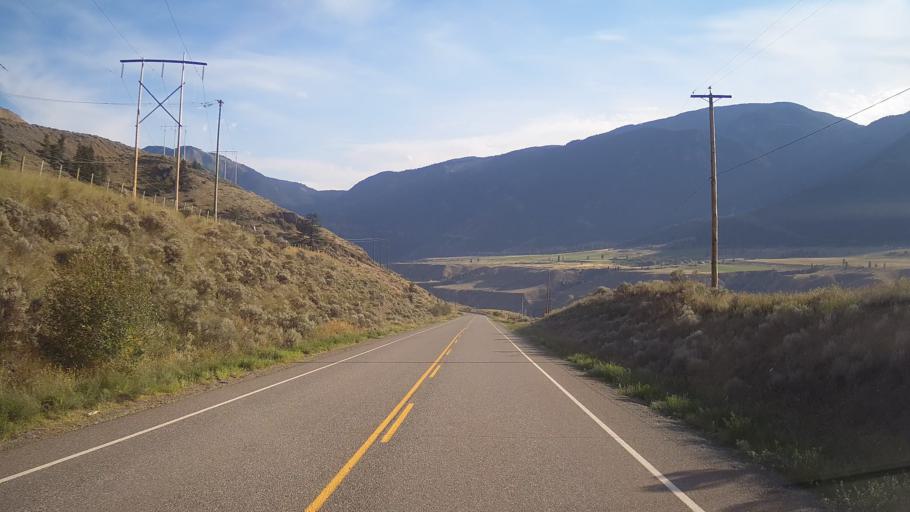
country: CA
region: British Columbia
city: Lillooet
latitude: 50.8593
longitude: -121.8575
